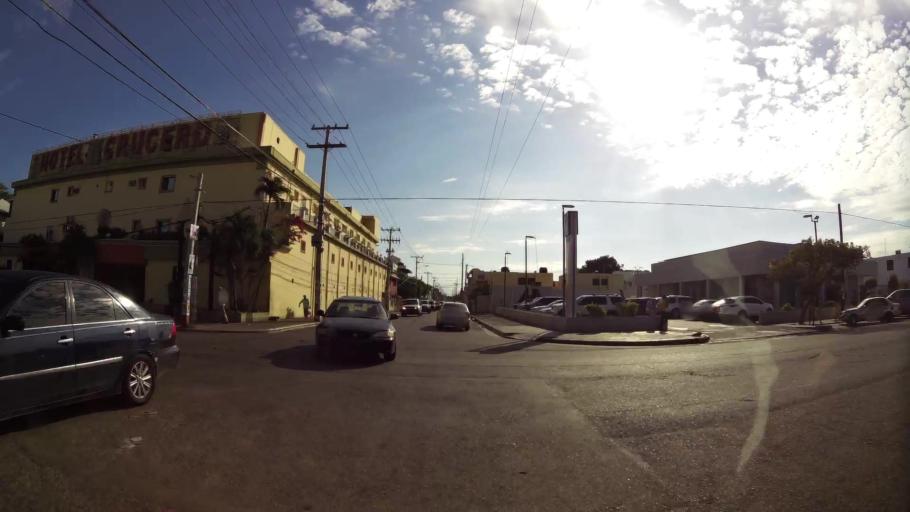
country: DO
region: Santo Domingo
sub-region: Santo Domingo
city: Santo Domingo Este
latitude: 18.4958
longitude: -69.8516
